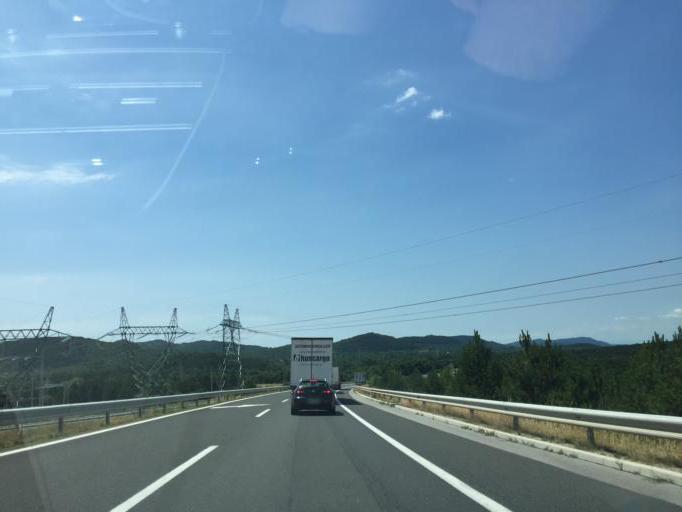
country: SI
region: Divaca
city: Divaca
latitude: 45.6943
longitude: 13.9737
